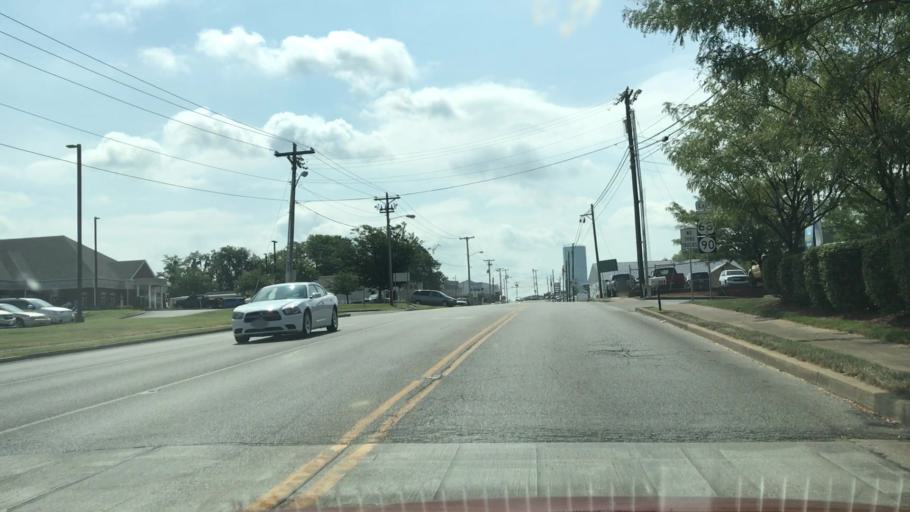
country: US
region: Kentucky
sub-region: Barren County
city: Glasgow
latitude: 37.0018
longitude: -85.9261
